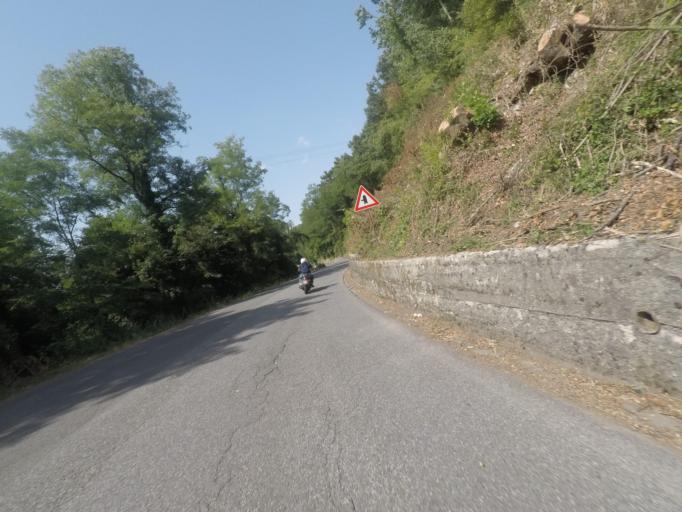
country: IT
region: Tuscany
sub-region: Provincia di Massa-Carrara
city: Fivizzano
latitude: 44.1720
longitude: 10.1152
